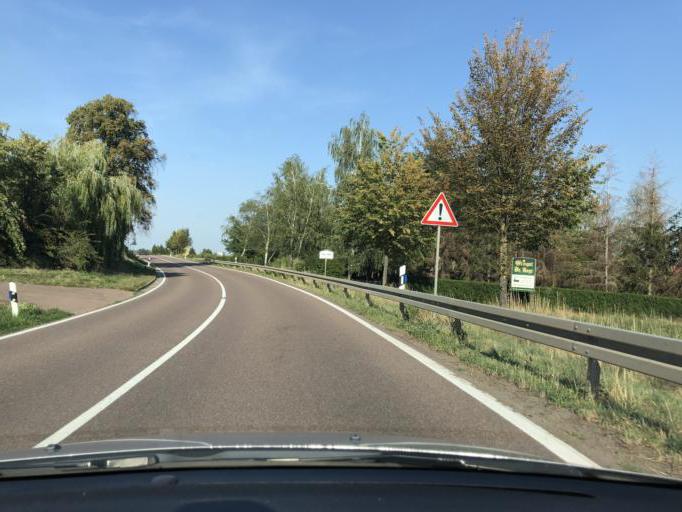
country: DE
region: Saxony-Anhalt
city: Goseck
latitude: 51.2360
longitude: 11.8234
